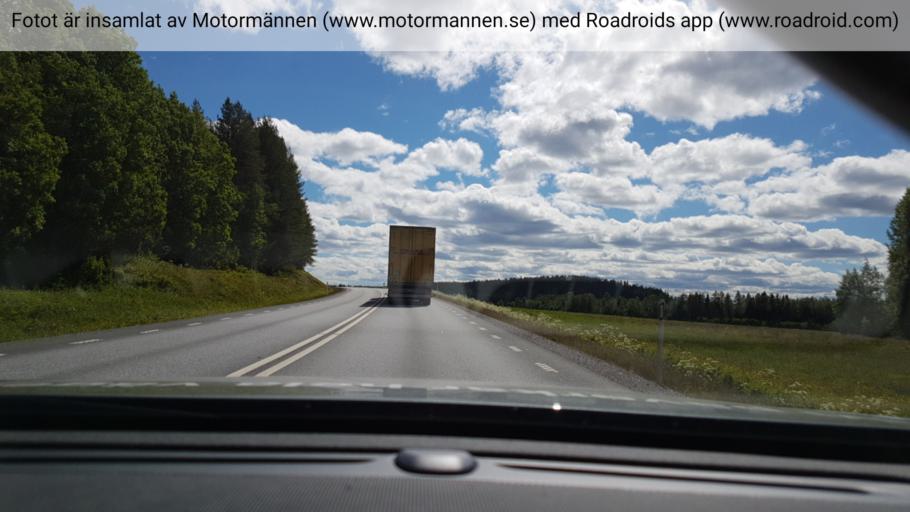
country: SE
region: Vaesterbotten
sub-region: Robertsfors Kommun
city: Robertsfors
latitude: 64.2199
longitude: 21.0151
